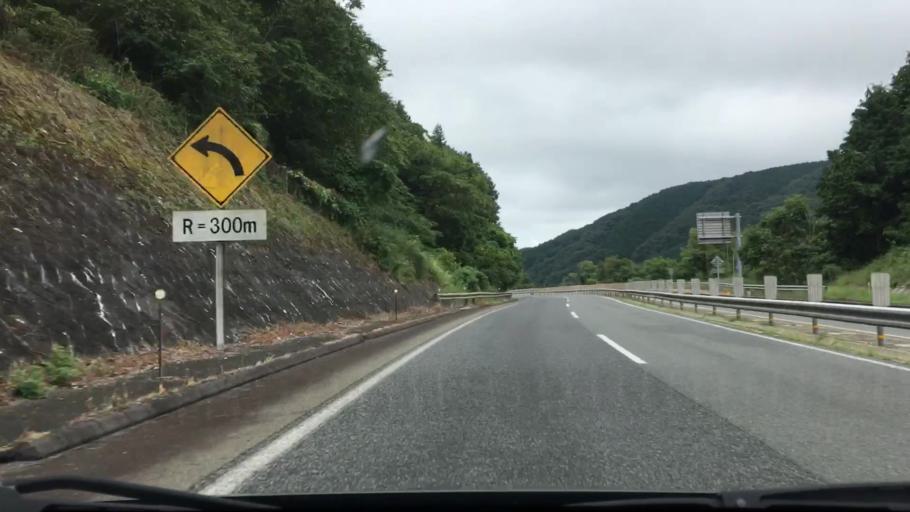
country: JP
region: Hiroshima
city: Shobara
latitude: 34.8426
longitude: 133.0859
